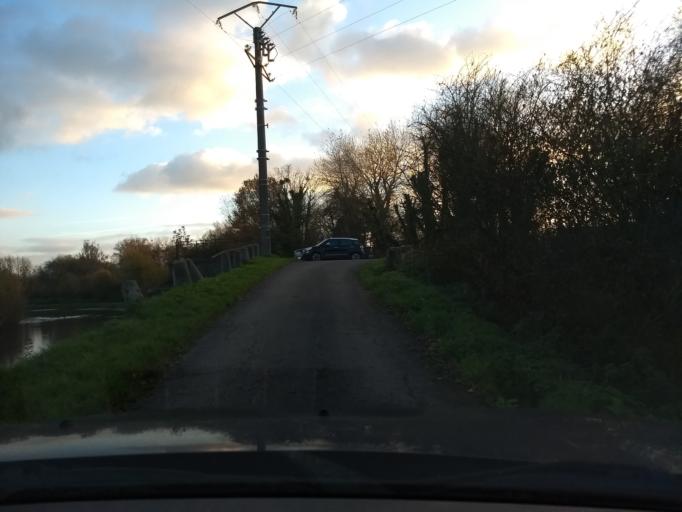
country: BE
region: Wallonia
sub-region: Province du Brabant Wallon
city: Ittre
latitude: 50.5894
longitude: 4.2523
